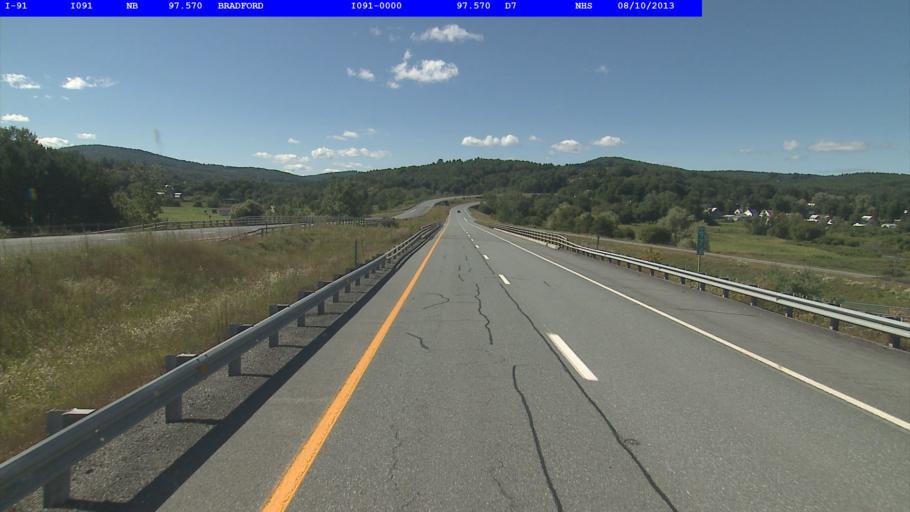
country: US
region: New Hampshire
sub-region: Grafton County
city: Orford
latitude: 43.9831
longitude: -72.1300
